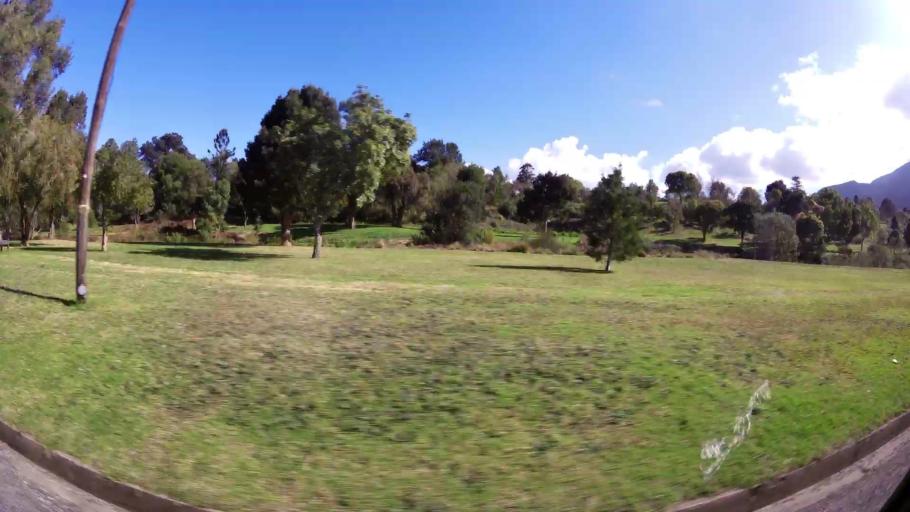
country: ZA
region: Western Cape
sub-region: Eden District Municipality
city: George
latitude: -33.9491
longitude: 22.4570
